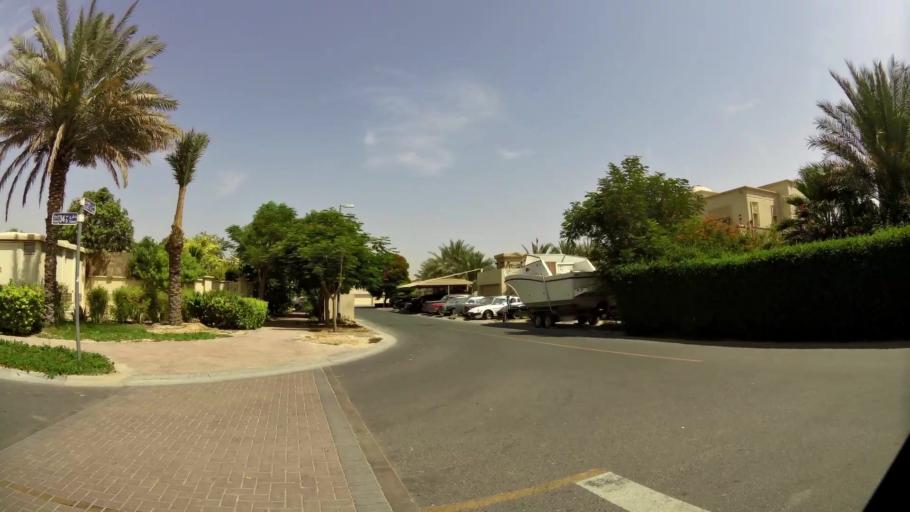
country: AE
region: Ash Shariqah
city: Sharjah
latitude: 25.1800
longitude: 55.4373
